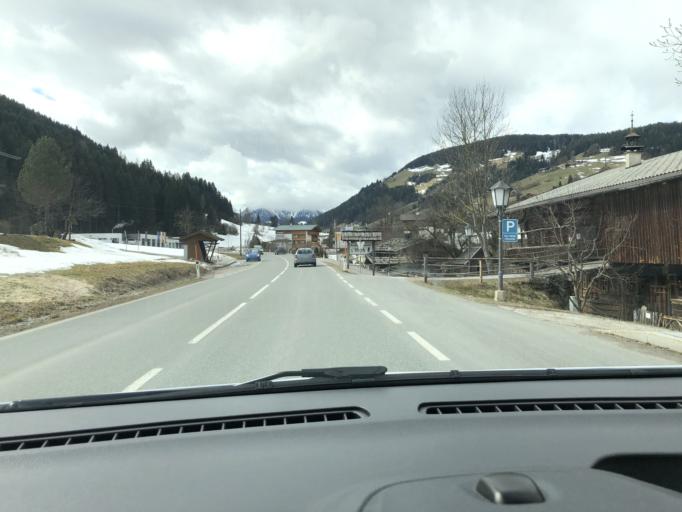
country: AT
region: Tyrol
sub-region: Politischer Bezirk Kufstein
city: Worgl
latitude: 47.4494
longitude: 12.0706
